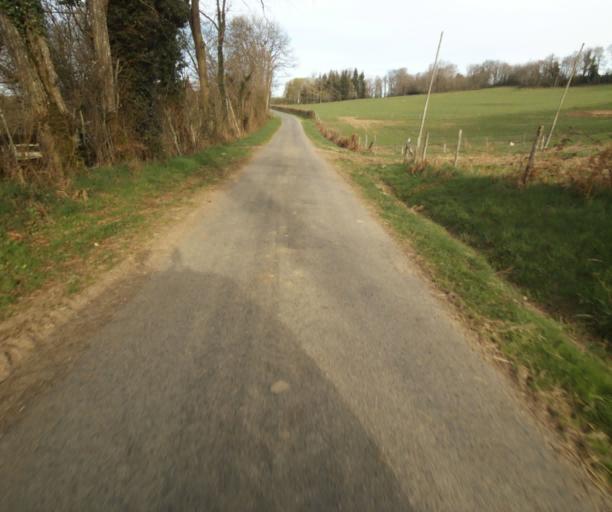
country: FR
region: Limousin
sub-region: Departement de la Correze
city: Chamboulive
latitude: 45.4489
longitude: 1.7534
